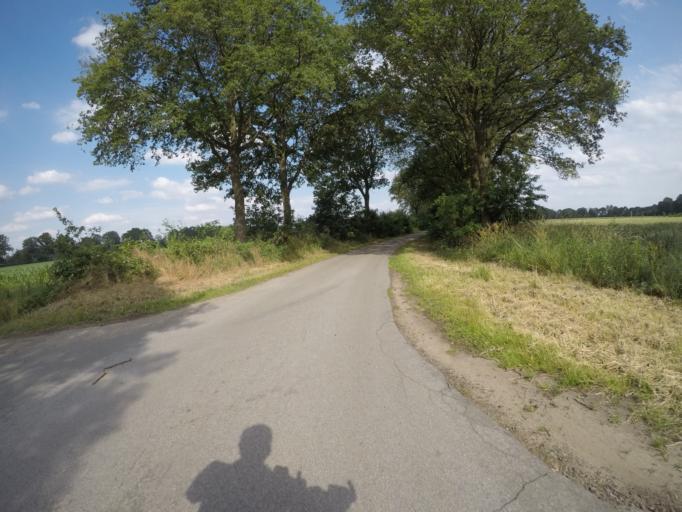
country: DE
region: North Rhine-Westphalia
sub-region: Regierungsbezirk Munster
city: Velen
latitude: 51.8809
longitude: 7.0833
